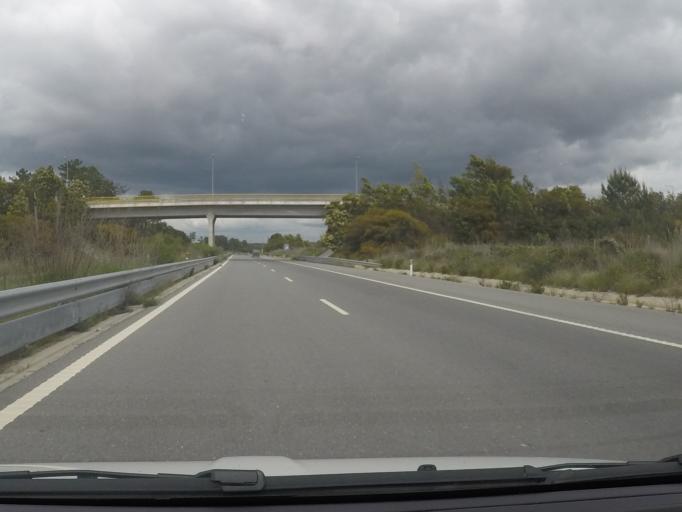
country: PT
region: Setubal
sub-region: Santiago do Cacem
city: Santo Andre
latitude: 37.9834
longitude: -8.7858
